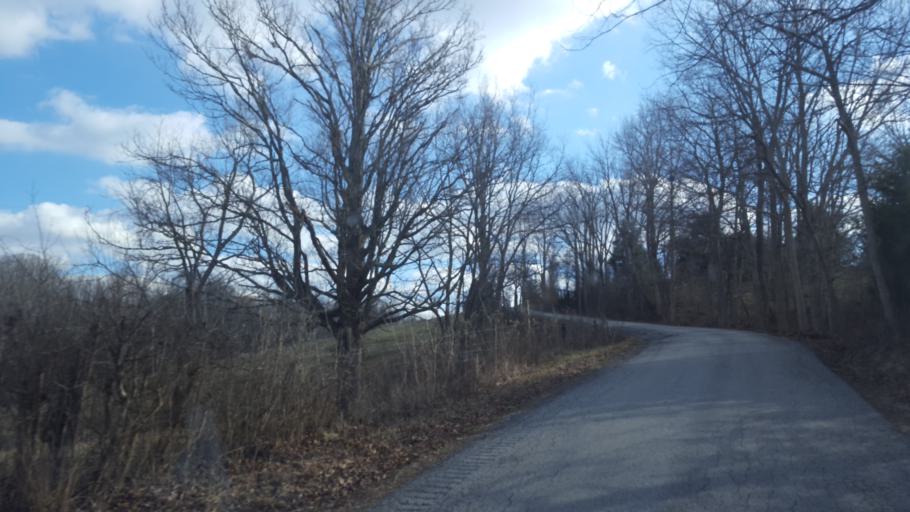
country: US
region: Kentucky
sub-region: Scott County
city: Georgetown
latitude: 38.3303
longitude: -84.5127
